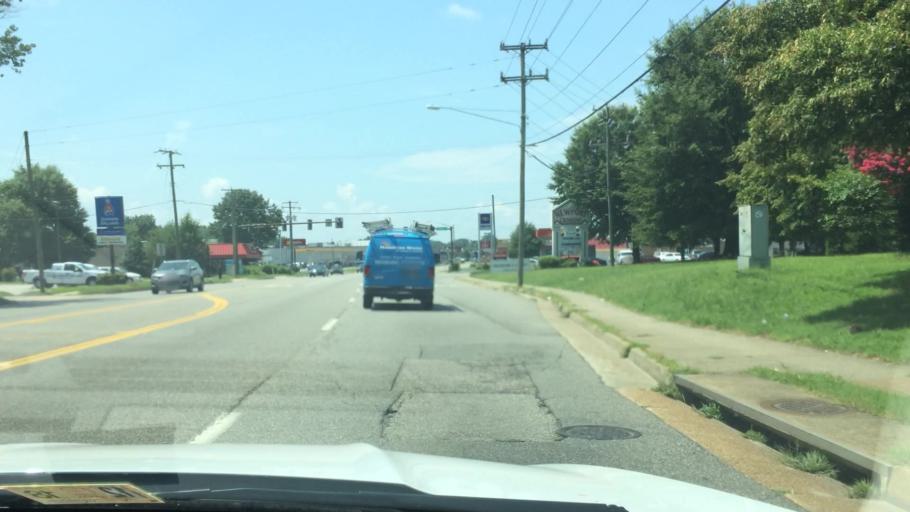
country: US
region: Virginia
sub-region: York County
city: Yorktown
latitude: 37.1322
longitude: -76.5319
